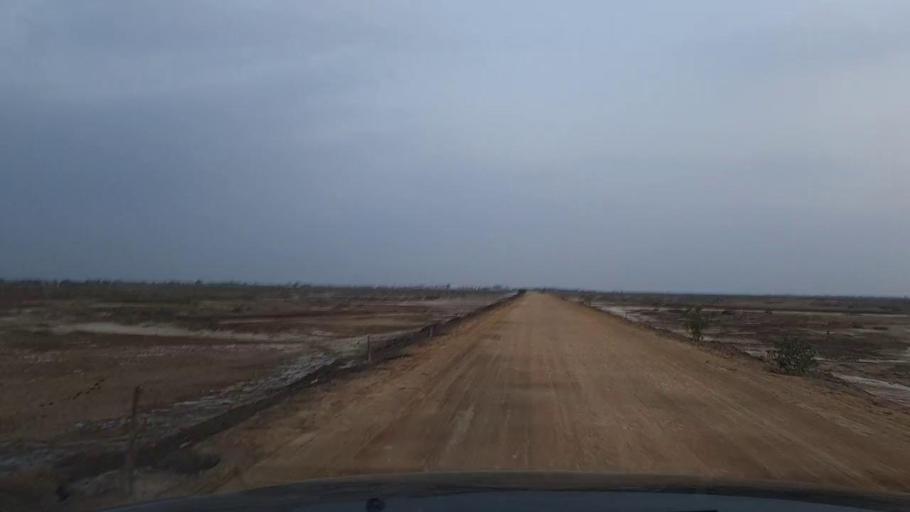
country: PK
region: Sindh
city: Jati
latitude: 24.4985
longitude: 68.3834
